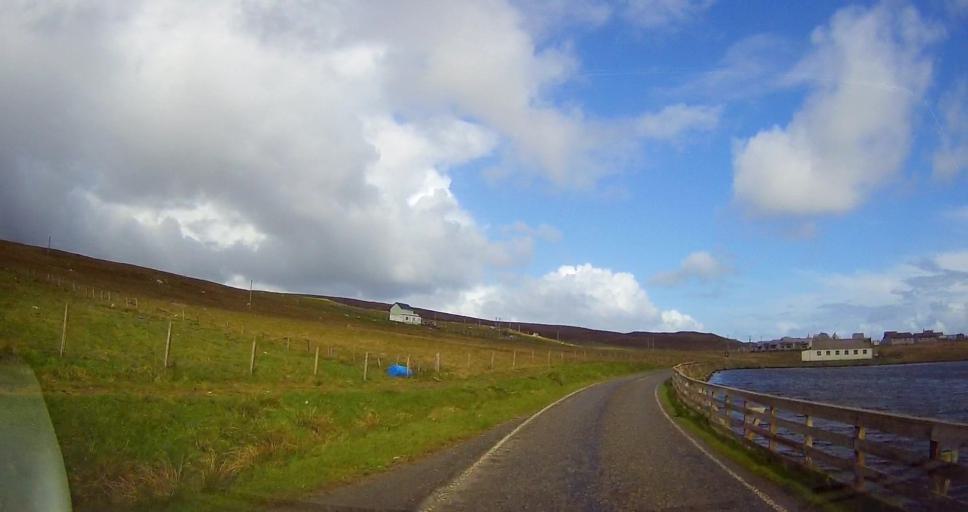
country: GB
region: Scotland
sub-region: Shetland Islands
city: Lerwick
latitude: 60.5832
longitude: -1.3361
